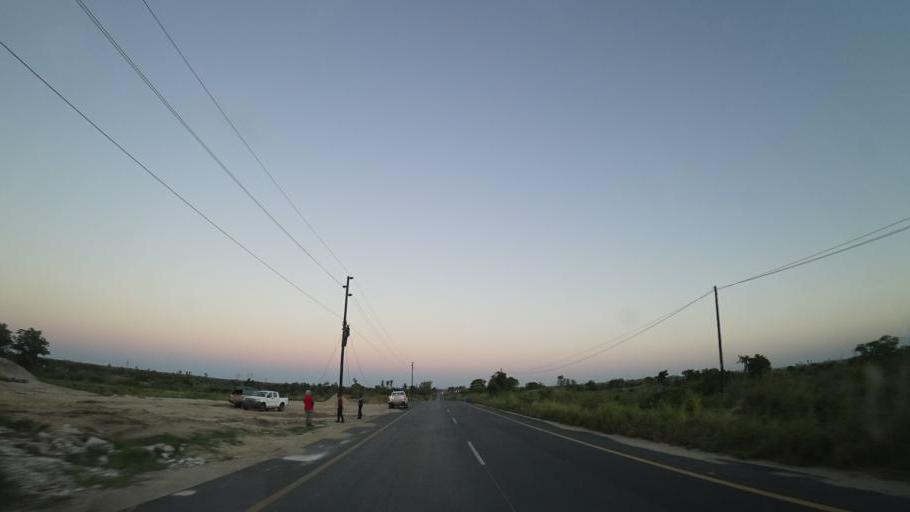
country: MZ
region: Sofala
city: Dondo
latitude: -19.5045
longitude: 34.6034
